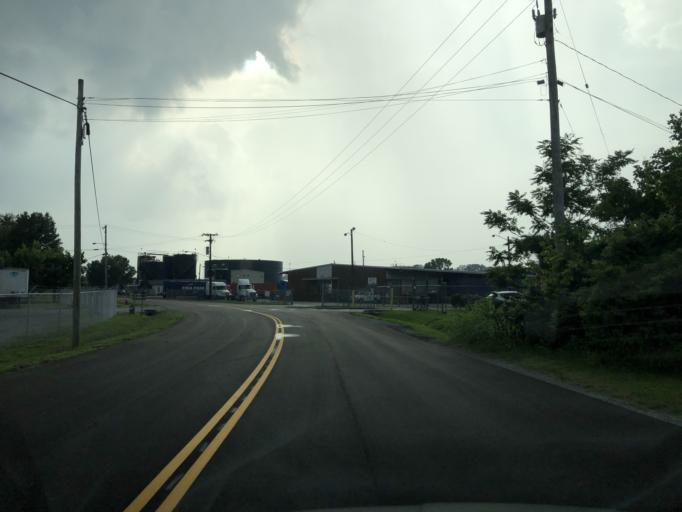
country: US
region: Tennessee
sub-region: Davidson County
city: Nashville
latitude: 36.1616
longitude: -86.7312
